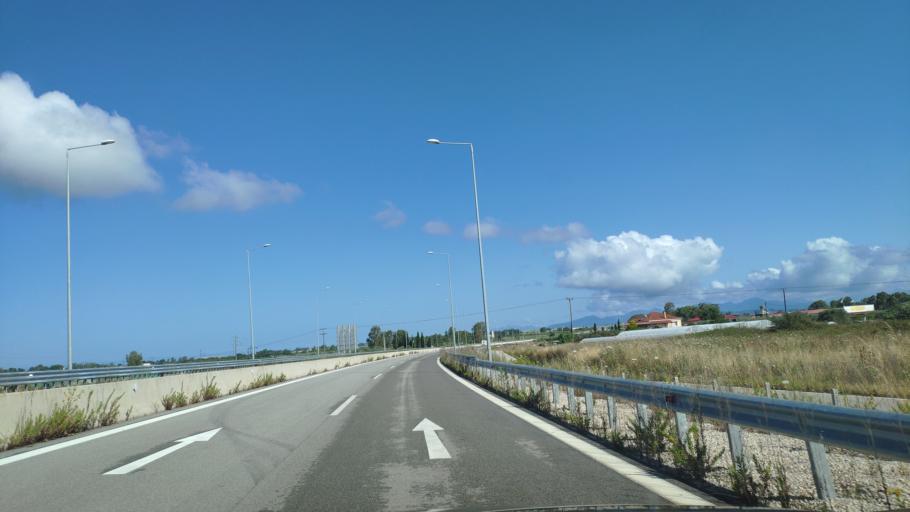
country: GR
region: Epirus
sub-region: Nomos Prevezis
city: Preveza
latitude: 38.9150
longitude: 20.7938
